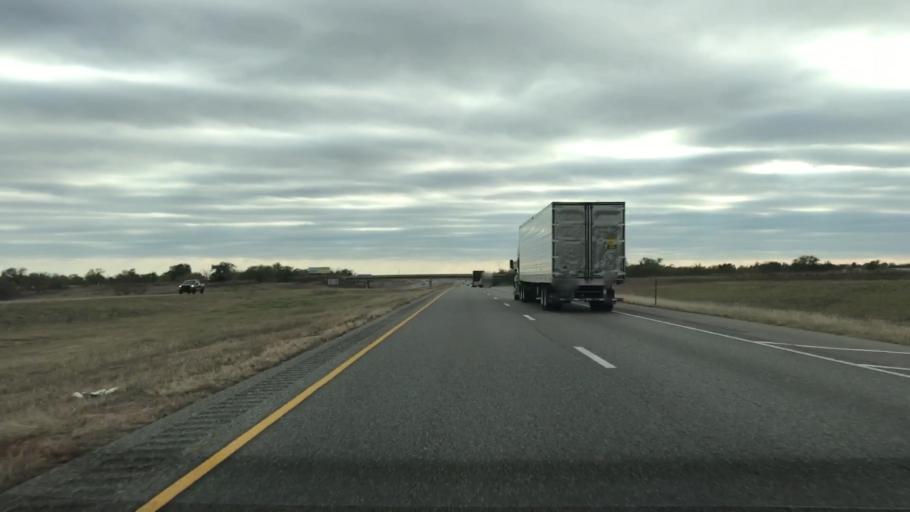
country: US
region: Oklahoma
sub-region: Beckham County
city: Sayre
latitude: 35.3098
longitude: -99.6149
